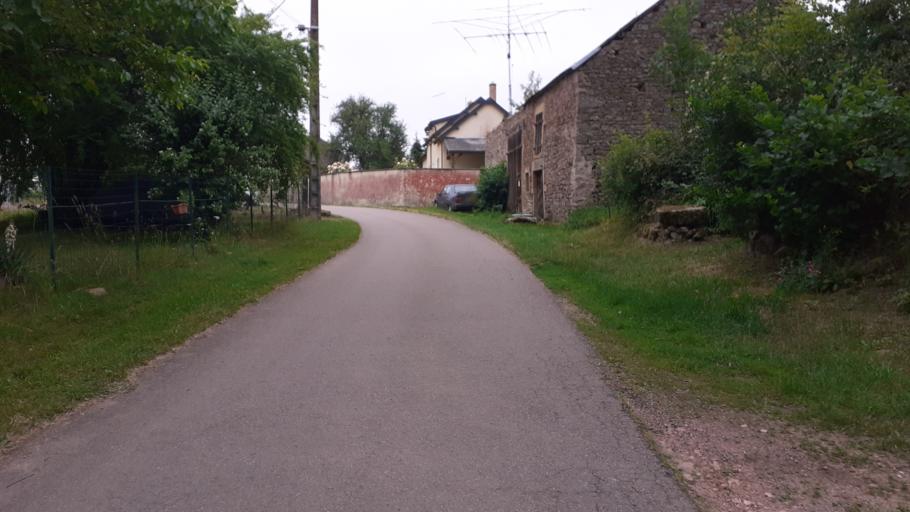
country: FR
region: Bourgogne
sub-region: Departement de la Cote-d'Or
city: Saulieu
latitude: 47.2706
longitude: 4.1347
